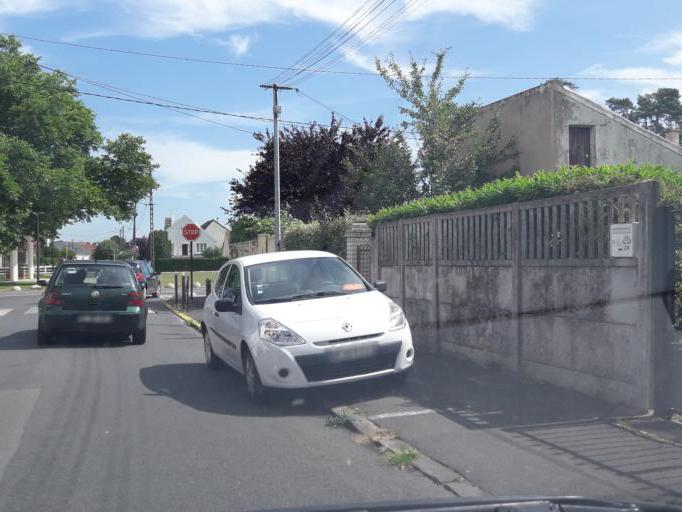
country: FR
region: Ile-de-France
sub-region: Departement de l'Essonne
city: Sainte-Genevieve-des-Bois
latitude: 48.6393
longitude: 2.3289
